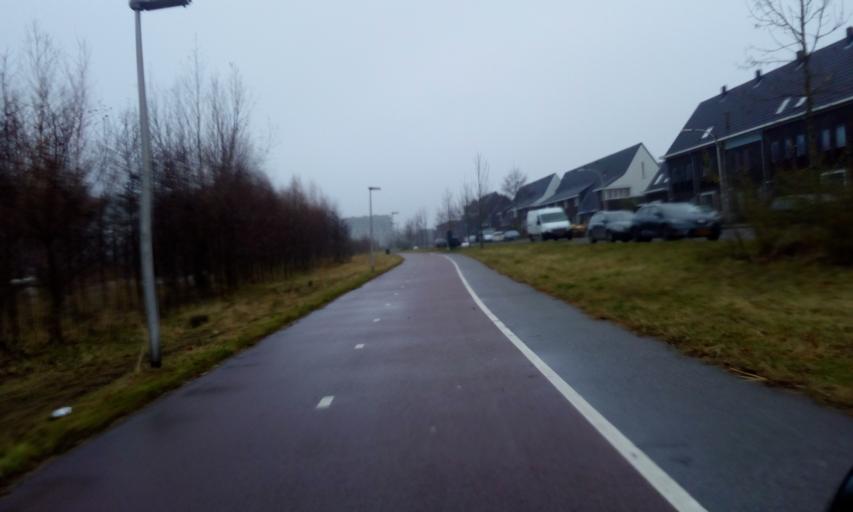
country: NL
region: South Holland
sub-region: Gemeente Pijnacker-Nootdorp
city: Pijnacker
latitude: 52.0075
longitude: 4.4391
